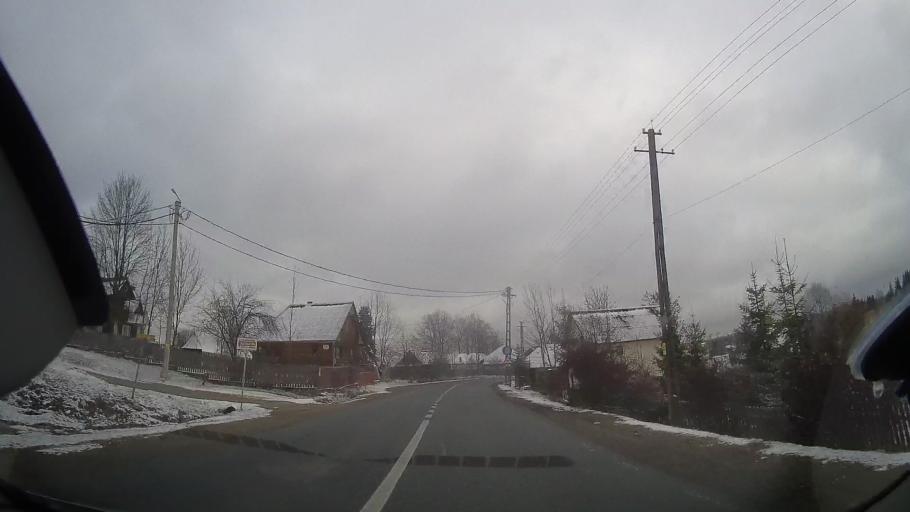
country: RO
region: Cluj
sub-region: Comuna Belis
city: Belis
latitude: 46.7071
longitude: 23.0381
